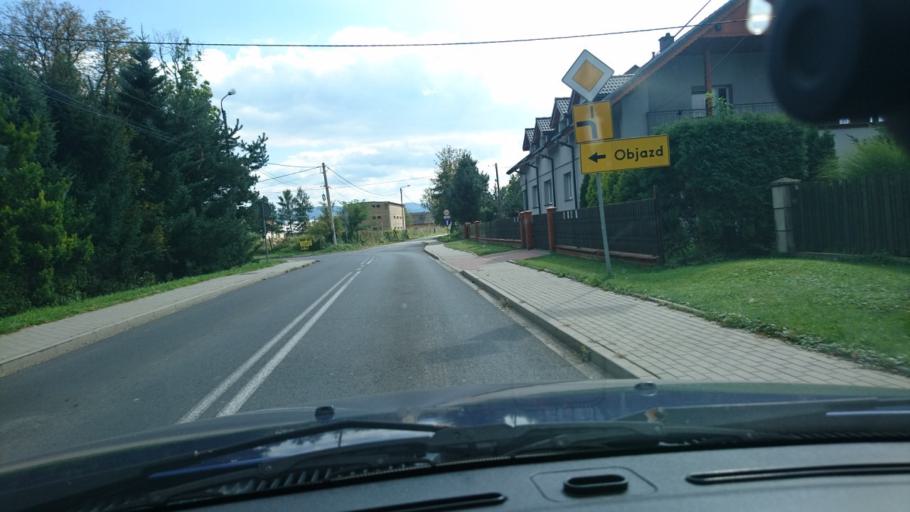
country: PL
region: Silesian Voivodeship
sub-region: Powiat bielski
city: Ligota
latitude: 49.8769
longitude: 18.9505
